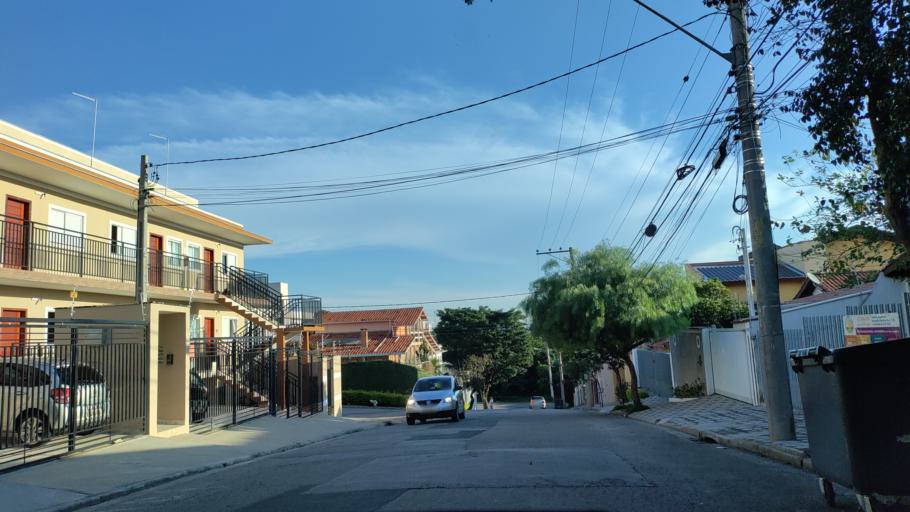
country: BR
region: Sao Paulo
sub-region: Sorocaba
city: Sorocaba
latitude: -23.5083
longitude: -47.4903
